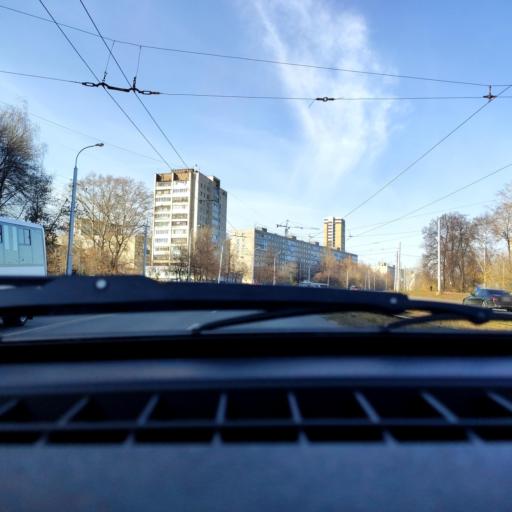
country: RU
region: Bashkortostan
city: Ufa
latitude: 54.8037
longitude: 56.1352
